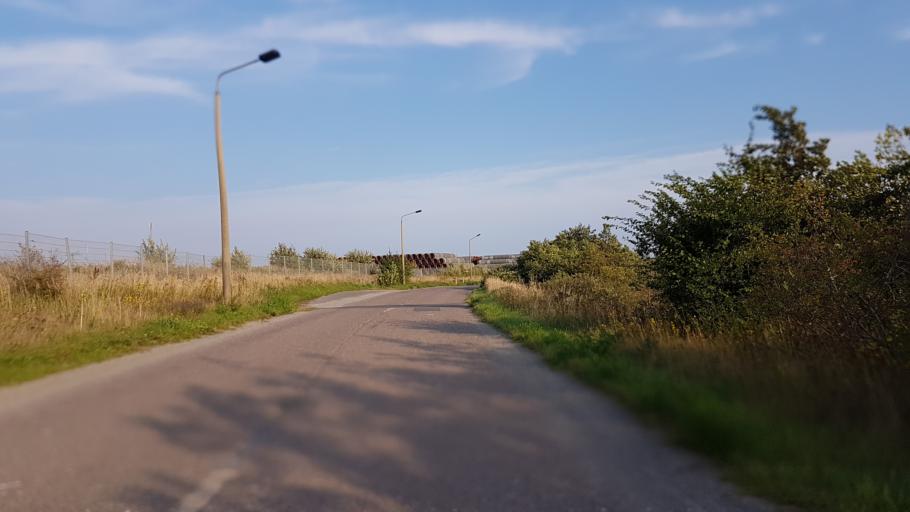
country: DE
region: Mecklenburg-Vorpommern
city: Sagard
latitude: 54.4921
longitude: 13.5678
